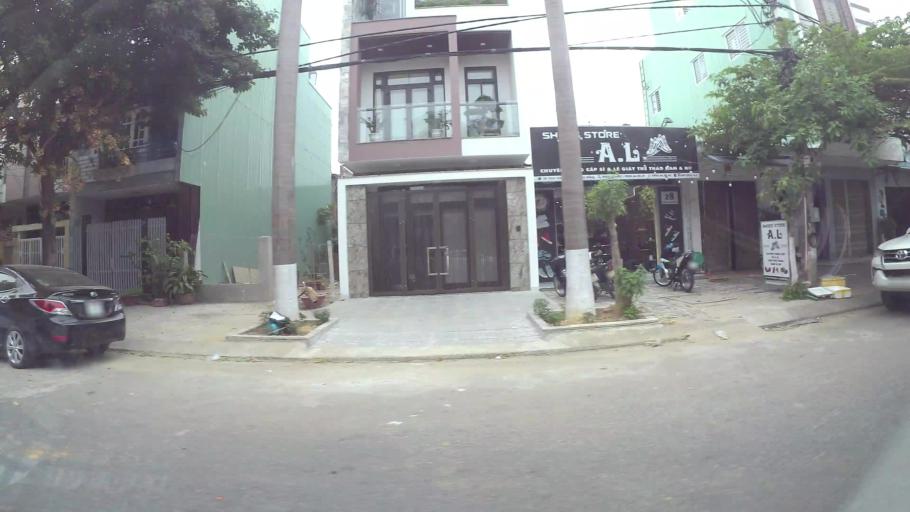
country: VN
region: Da Nang
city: Cam Le
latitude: 16.0352
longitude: 108.2203
